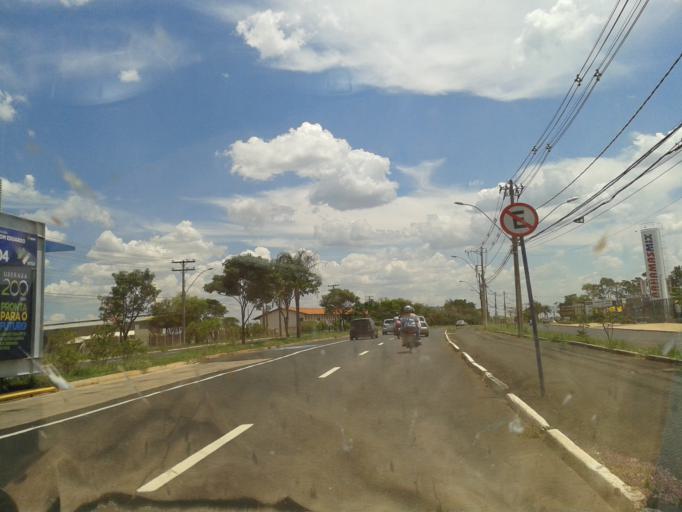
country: BR
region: Minas Gerais
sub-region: Uberaba
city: Uberaba
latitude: -19.7487
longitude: -47.9714
